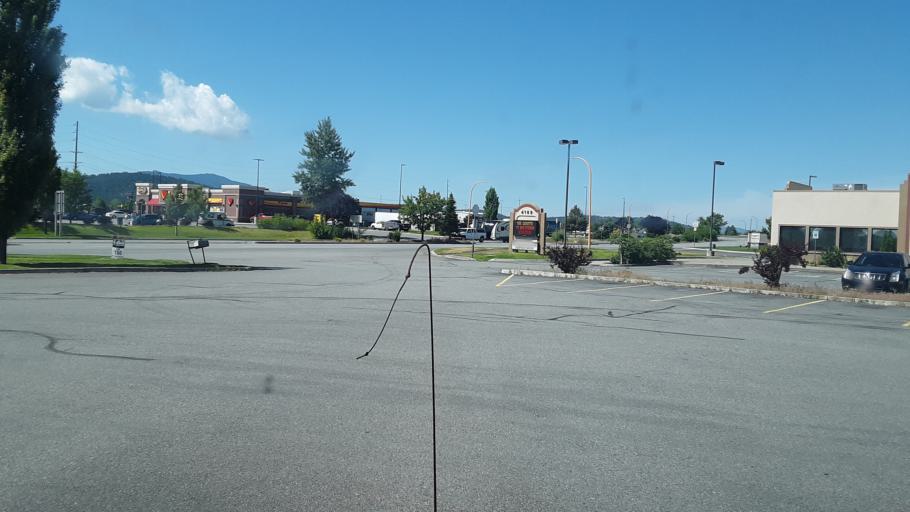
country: US
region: Idaho
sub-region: Kootenai County
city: Post Falls
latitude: 47.7125
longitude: -117.0025
